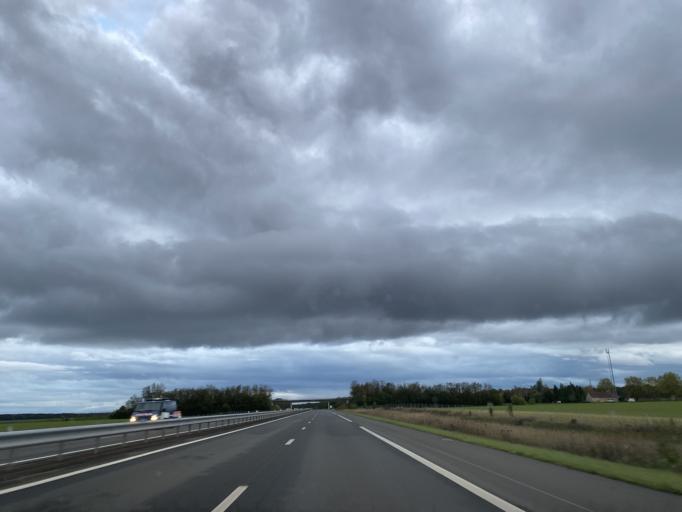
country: FR
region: Centre
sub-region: Departement du Cher
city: Levet
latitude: 46.8981
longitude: 2.4170
